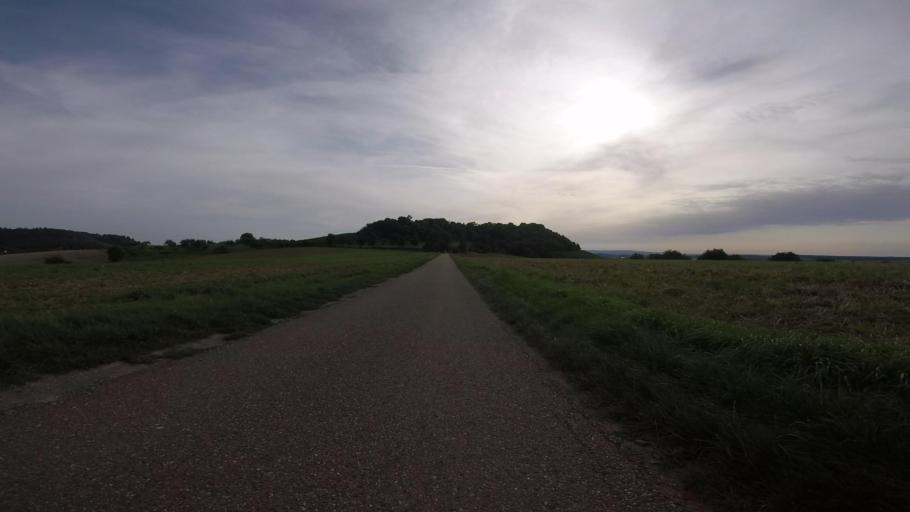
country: DE
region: Baden-Wuerttemberg
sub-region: Regierungsbezirk Stuttgart
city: Beilstein
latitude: 49.0660
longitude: 9.3169
